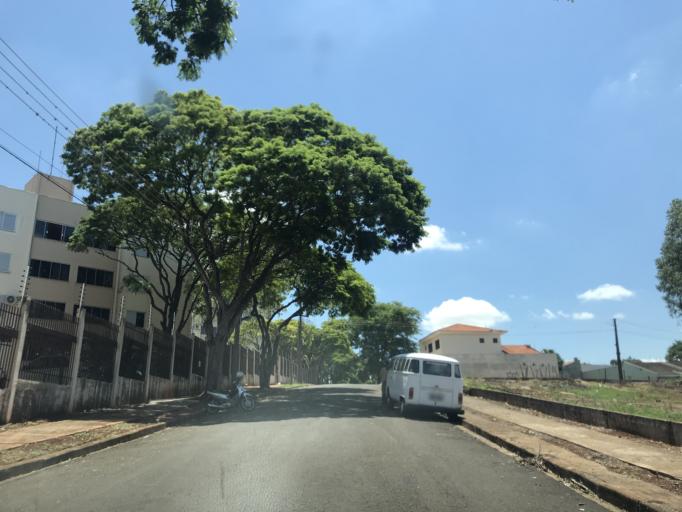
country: BR
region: Parana
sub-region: Maringa
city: Maringa
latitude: -23.4494
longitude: -51.9346
